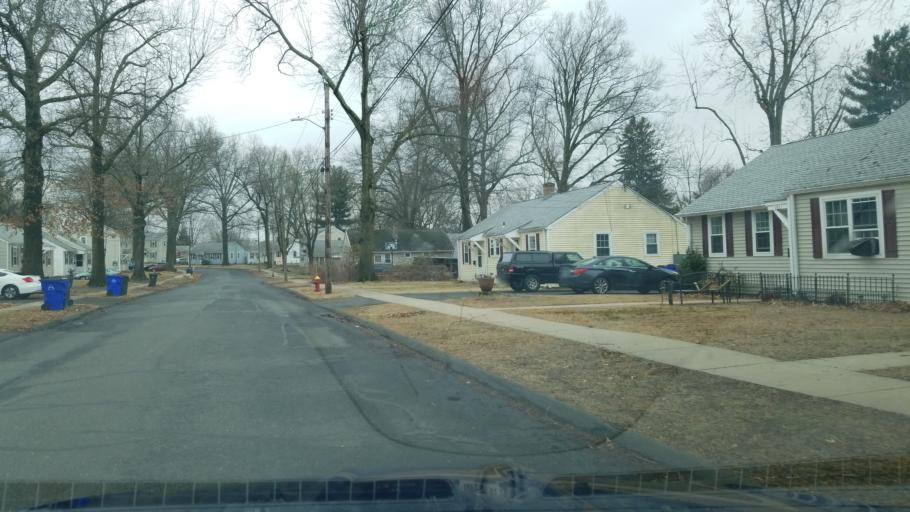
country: US
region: Connecticut
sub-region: Hartford County
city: Wethersfield
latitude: 41.6986
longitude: -72.6643
